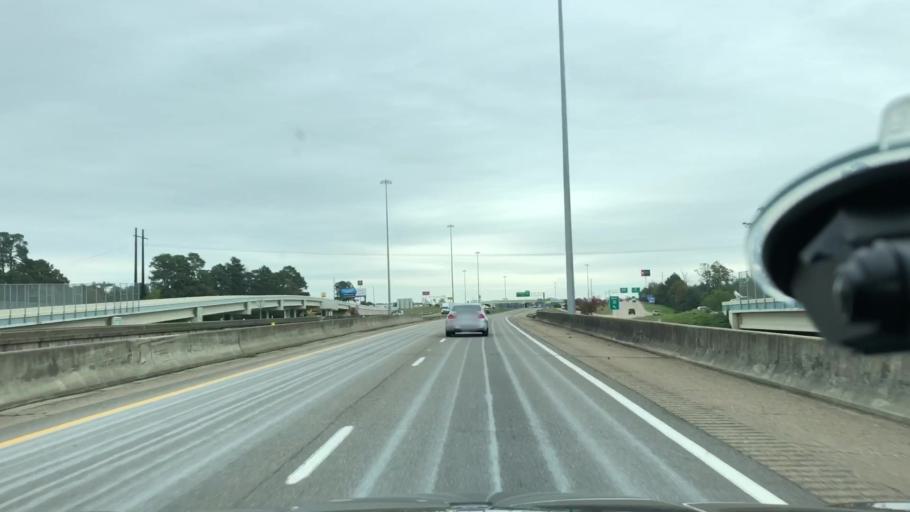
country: US
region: Arkansas
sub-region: Miller County
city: Texarkana
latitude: 33.4700
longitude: -94.0511
